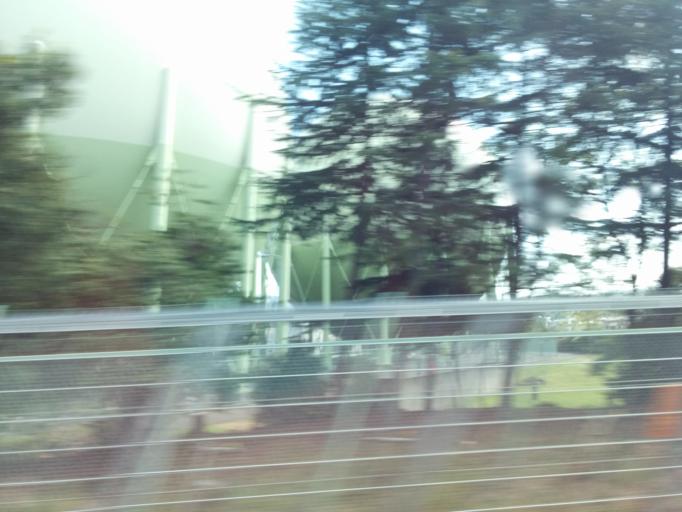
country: JP
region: Shiga Prefecture
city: Kusatsu
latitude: 34.9998
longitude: 135.9630
